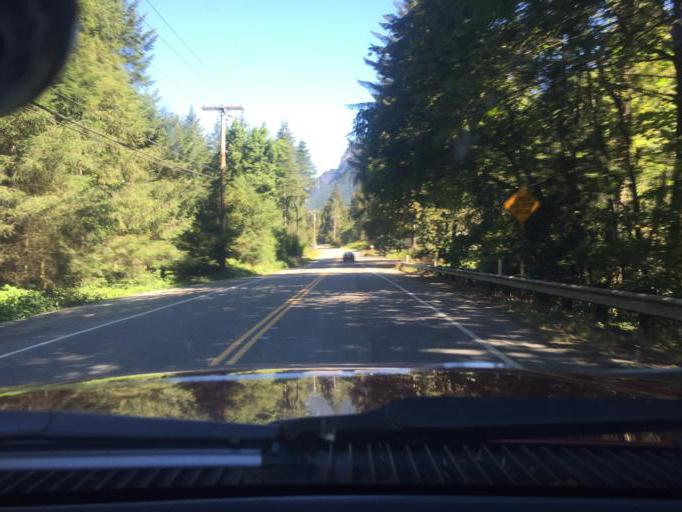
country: US
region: Washington
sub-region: King County
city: Riverbend
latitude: 47.4665
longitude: -121.7588
